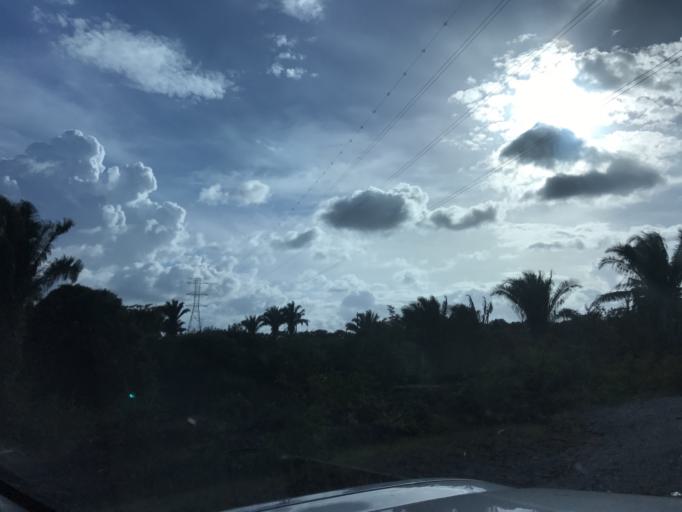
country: GT
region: Izabal
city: Morales
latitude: 15.6260
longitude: -89.0578
